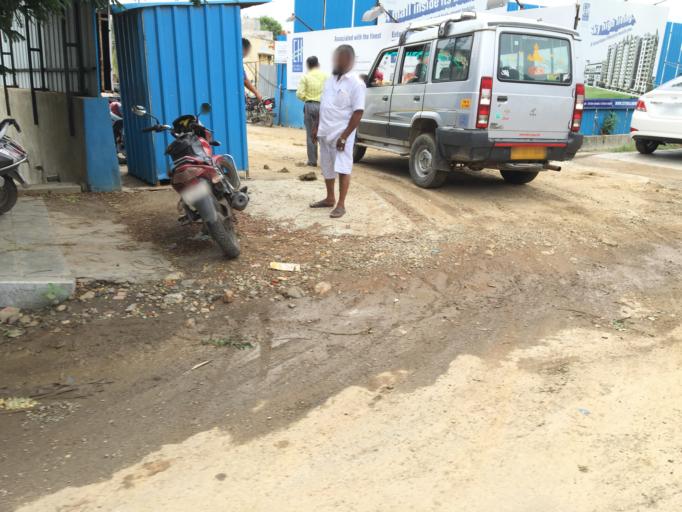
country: IN
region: Tamil Nadu
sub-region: Kancheepuram
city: Madipakkam
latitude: 12.9736
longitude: 80.2104
